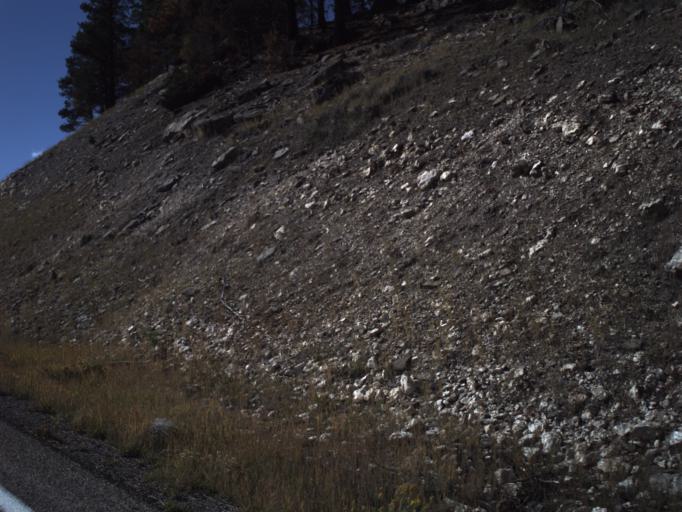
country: US
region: Utah
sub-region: Iron County
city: Parowan
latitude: 37.6508
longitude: -112.6933
